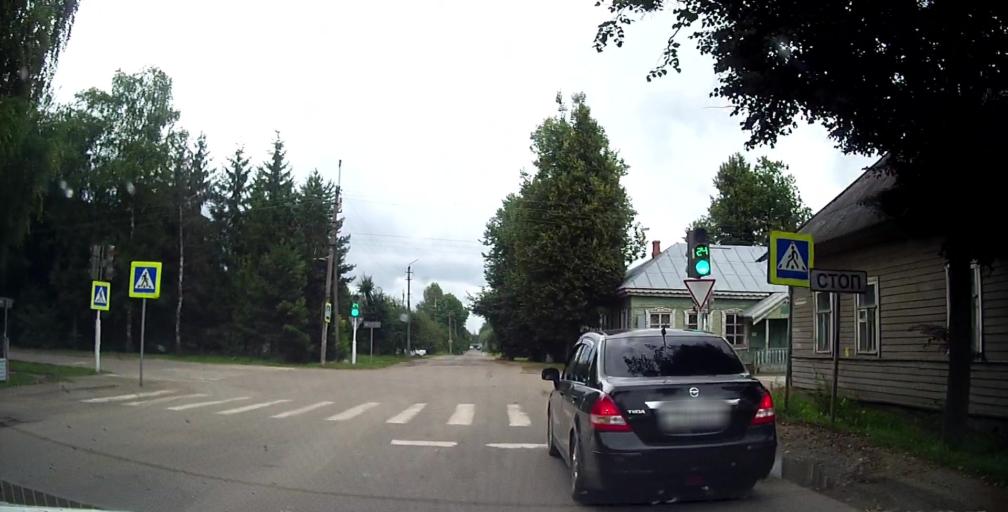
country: RU
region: Smolensk
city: Demidov
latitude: 55.2630
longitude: 31.5179
